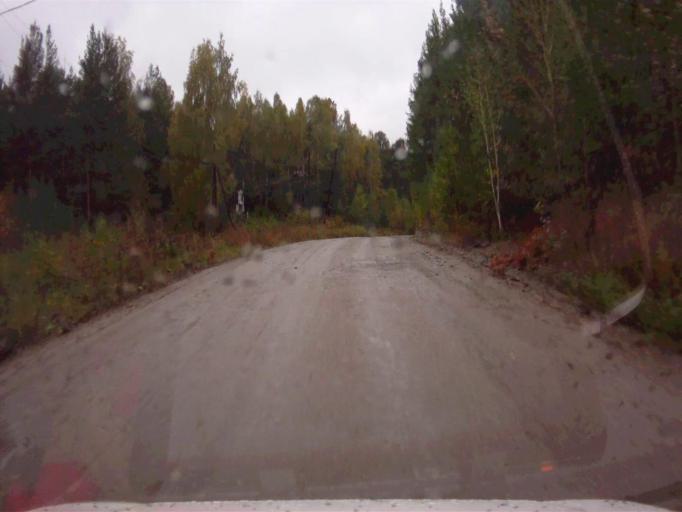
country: RU
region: Chelyabinsk
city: Kyshtym
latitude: 55.7435
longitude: 60.4934
